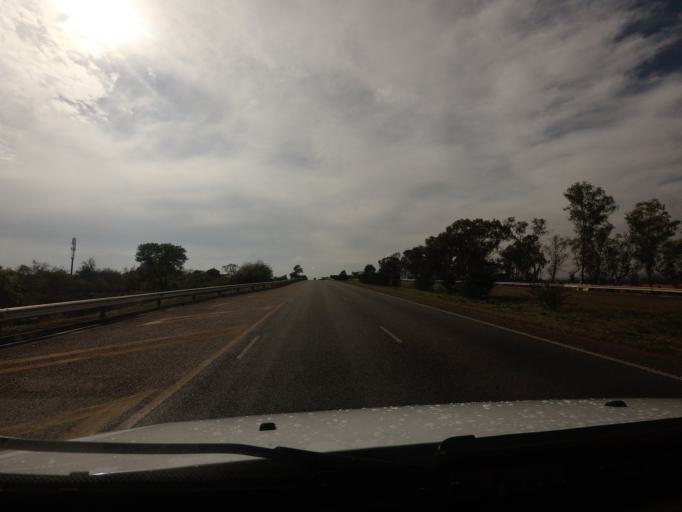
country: ZA
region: Gauteng
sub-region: City of Tshwane Metropolitan Municipality
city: Pretoria
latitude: -25.7547
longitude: 28.3402
